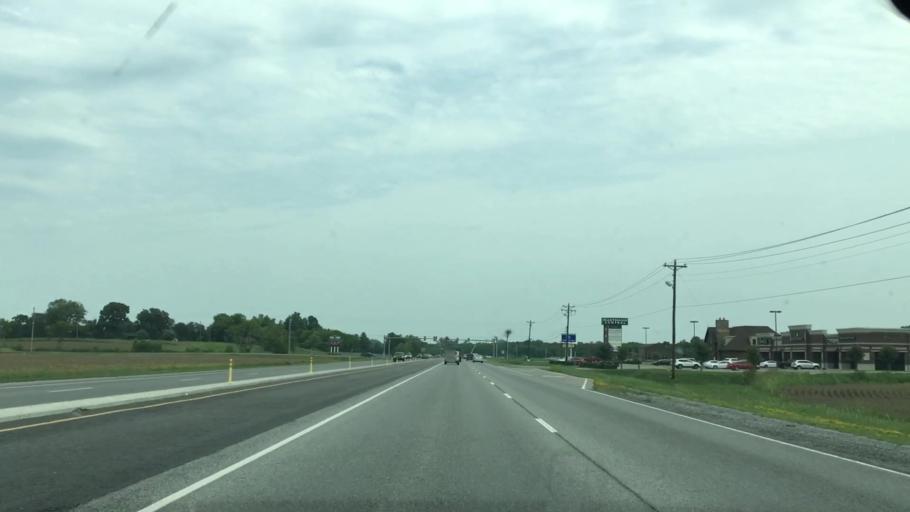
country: US
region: Tennessee
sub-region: Wilson County
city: Lebanon
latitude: 36.2011
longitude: -86.3296
